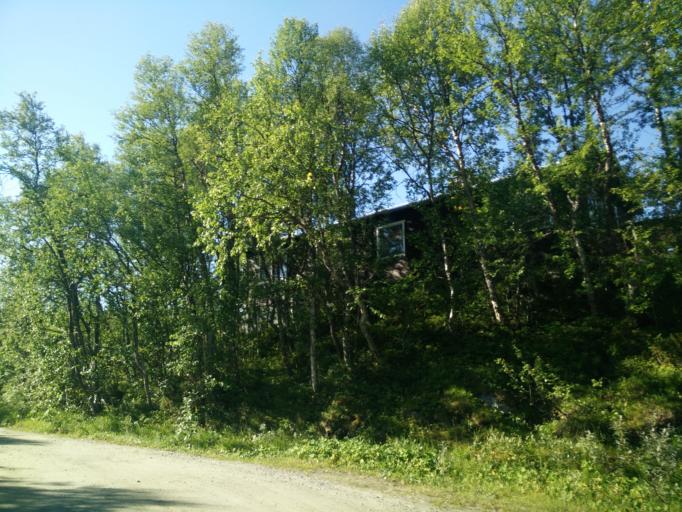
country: NO
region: Sor-Trondelag
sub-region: Tydal
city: Aas
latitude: 62.5789
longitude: 12.2089
